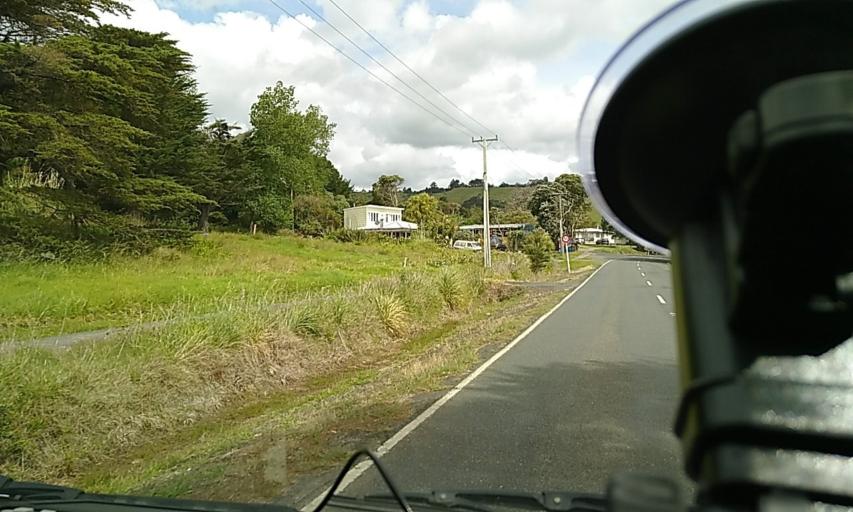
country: NZ
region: Northland
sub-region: Far North District
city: Ahipara
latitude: -35.5240
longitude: 173.3897
